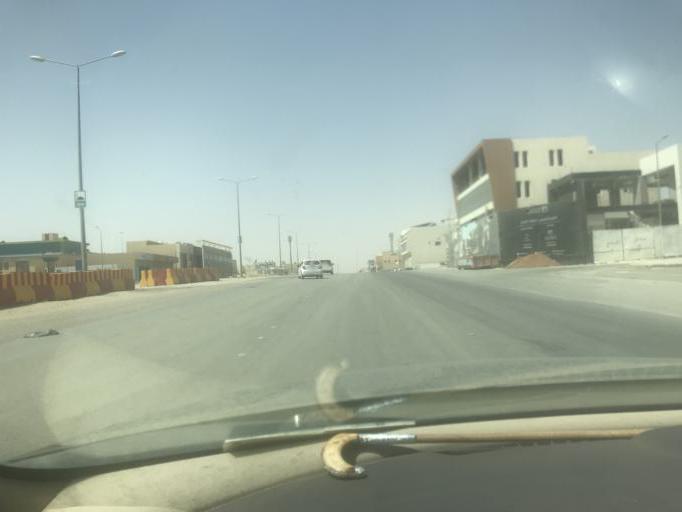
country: SA
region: Ar Riyad
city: Riyadh
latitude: 24.8166
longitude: 46.5975
